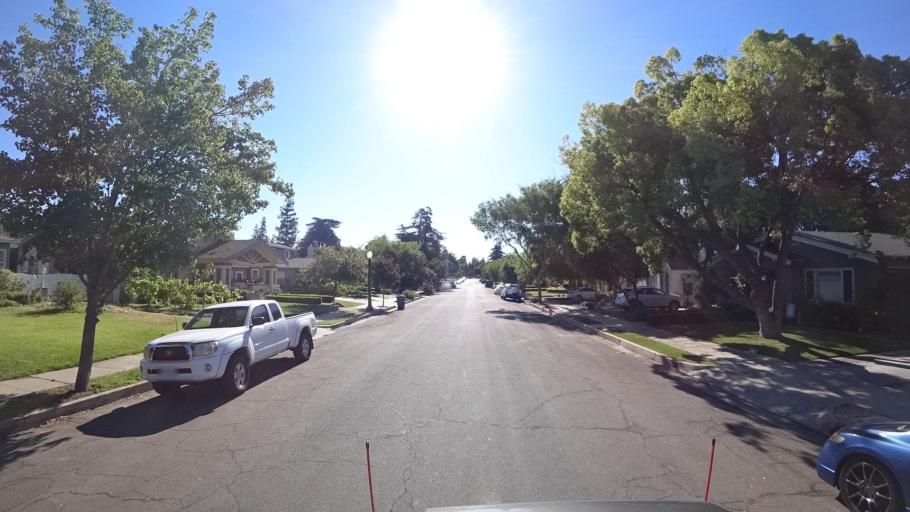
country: US
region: California
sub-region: Fresno County
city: Fresno
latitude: 36.7668
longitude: -119.8025
